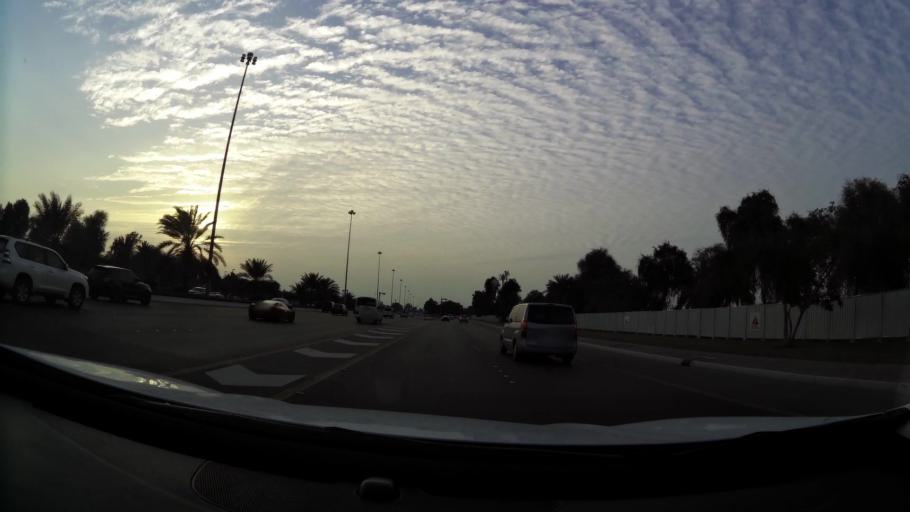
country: AE
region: Abu Dhabi
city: Abu Dhabi
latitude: 24.4308
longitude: 54.3881
